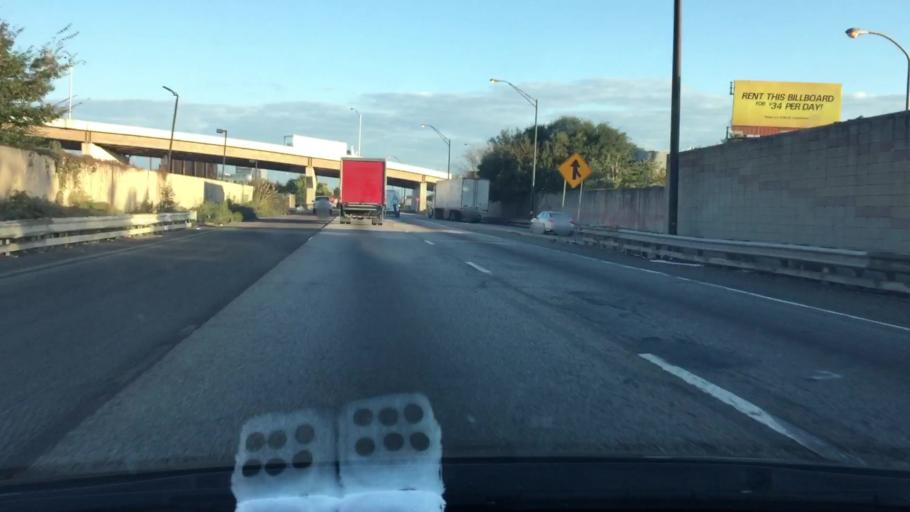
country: US
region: Pennsylvania
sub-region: Philadelphia County
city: Philadelphia
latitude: 39.9558
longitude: -75.1408
